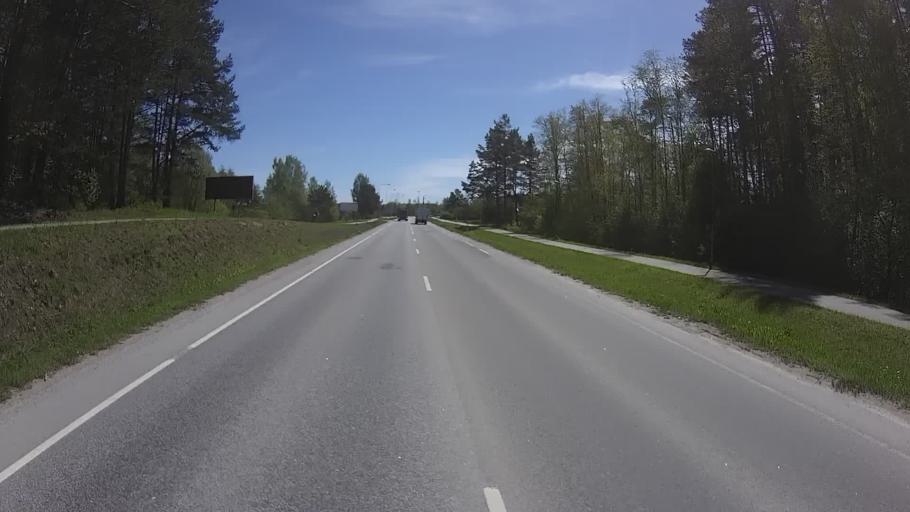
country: EE
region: Vorumaa
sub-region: Voru linn
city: Voru
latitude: 57.8181
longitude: 27.0260
